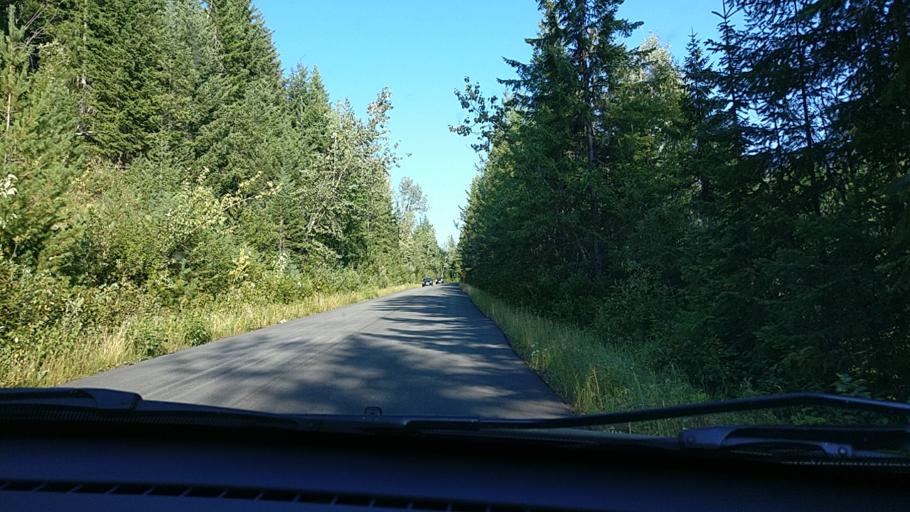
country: CA
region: British Columbia
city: Revelstoke
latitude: 51.0077
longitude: -118.1761
